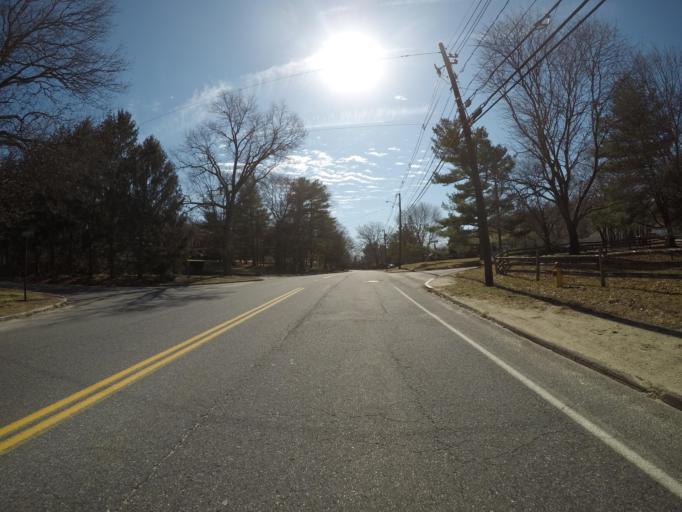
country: US
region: Massachusetts
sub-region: Norfolk County
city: Stoughton
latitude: 42.1109
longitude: -71.1336
